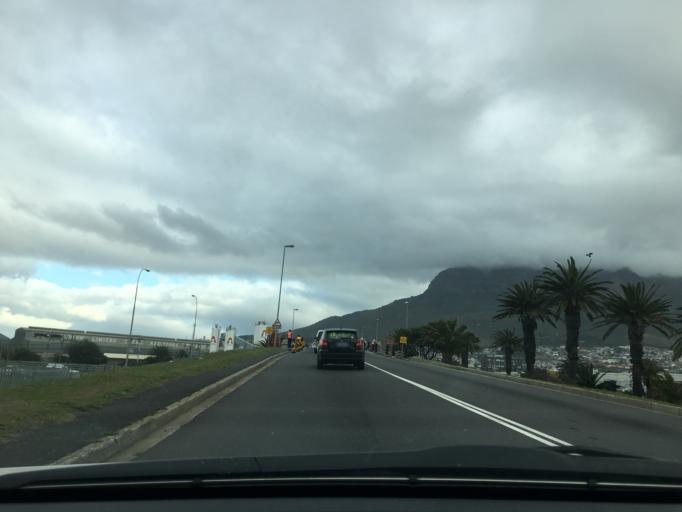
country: ZA
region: Western Cape
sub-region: City of Cape Town
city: Cape Town
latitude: -33.9202
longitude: 18.4567
